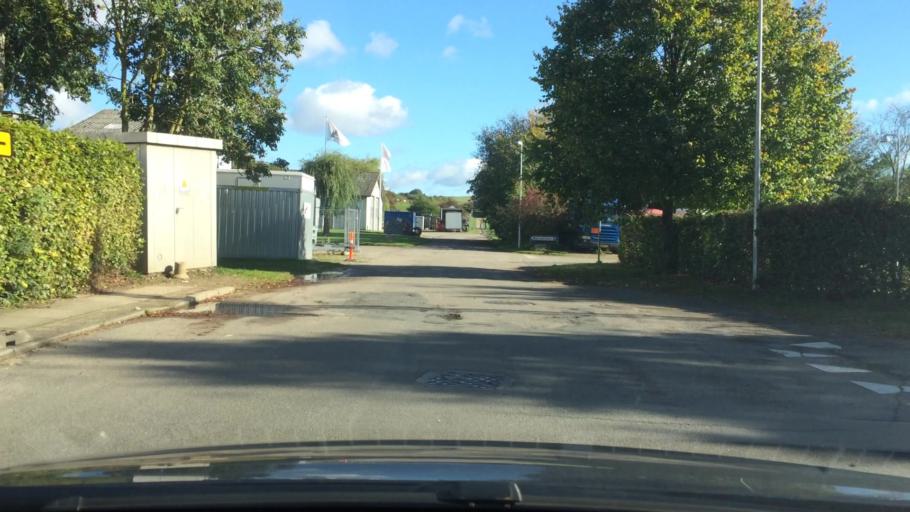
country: DK
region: Central Jutland
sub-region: Horsens Kommune
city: Horsens
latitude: 55.8759
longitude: 9.9198
